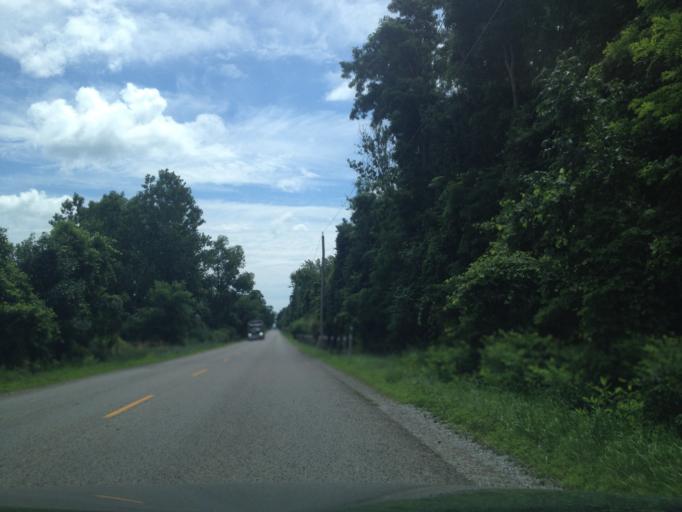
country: CA
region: Ontario
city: Norfolk County
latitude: 42.8015
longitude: -80.3139
